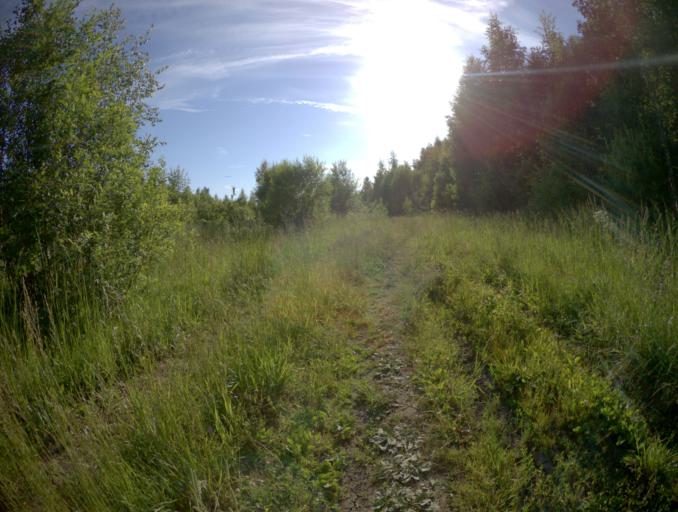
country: RU
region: Vladimir
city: Vladimir
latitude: 56.1578
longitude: 40.2252
